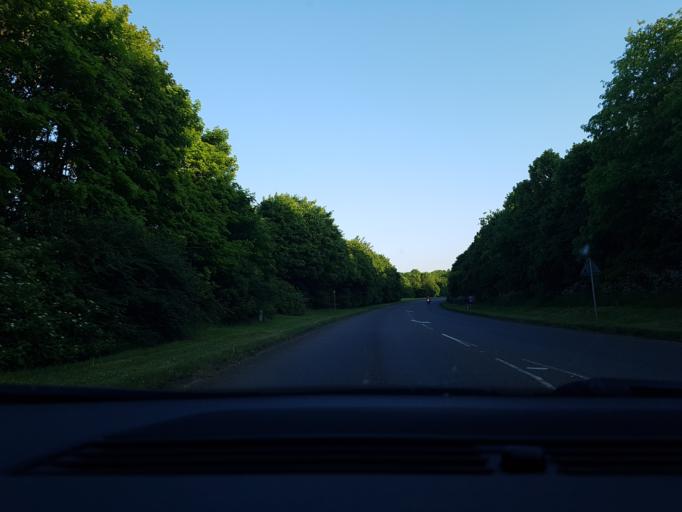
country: GB
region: England
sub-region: Buckinghamshire
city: Buckingham
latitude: 51.9998
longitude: -0.9700
